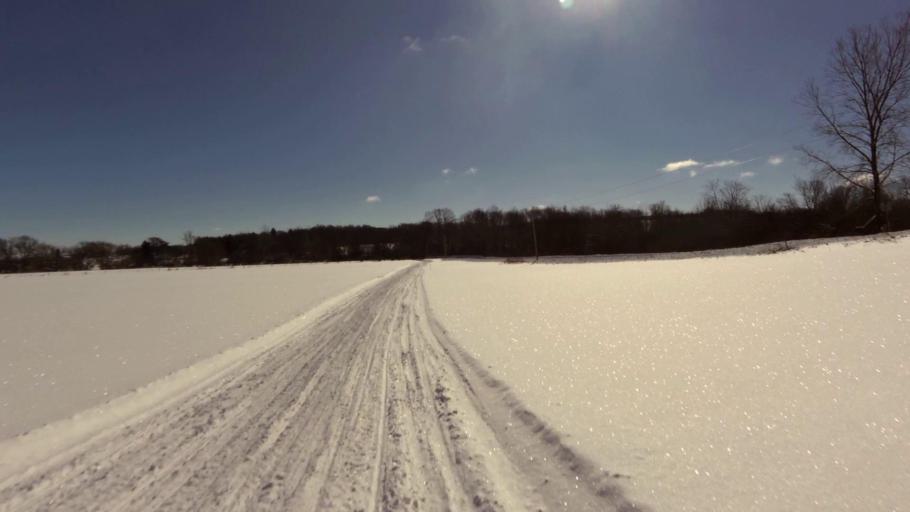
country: US
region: New York
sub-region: Chautauqua County
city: Fredonia
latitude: 42.3666
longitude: -79.1739
